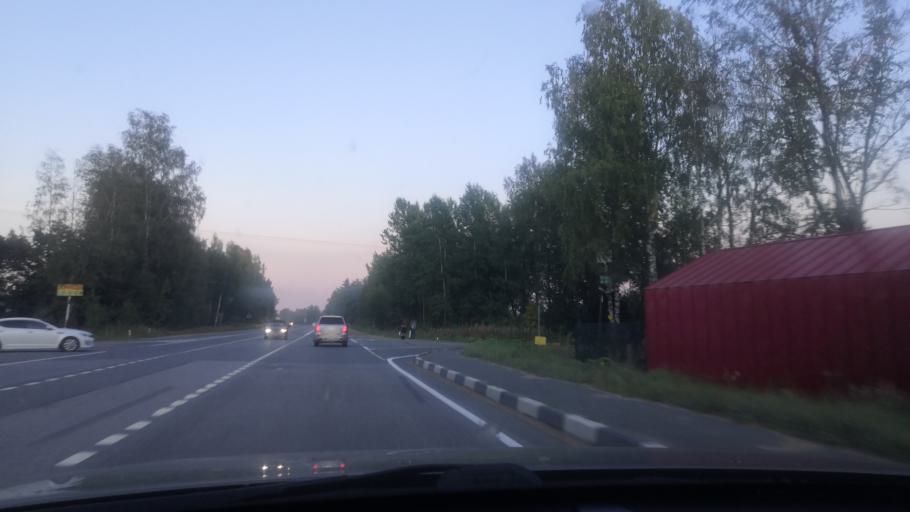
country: RU
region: St.-Petersburg
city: Beloostrov
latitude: 60.1983
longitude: 30.0070
